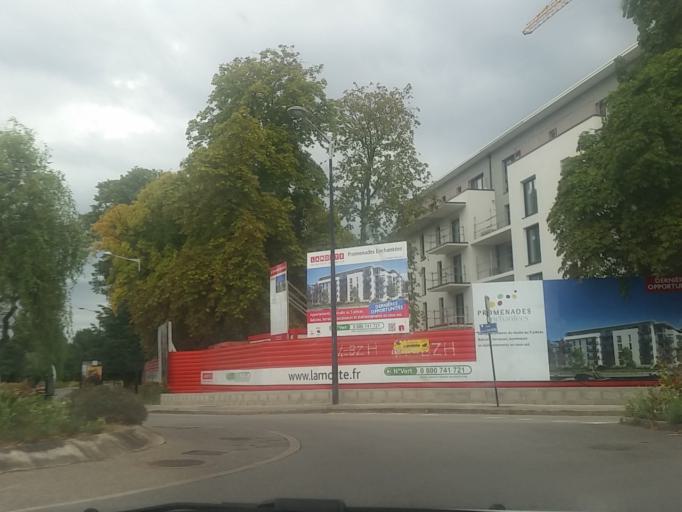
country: FR
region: Pays de la Loire
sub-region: Departement de la Loire-Atlantique
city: Saint-Sebastien-sur-Loire
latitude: 47.2074
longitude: -1.5184
